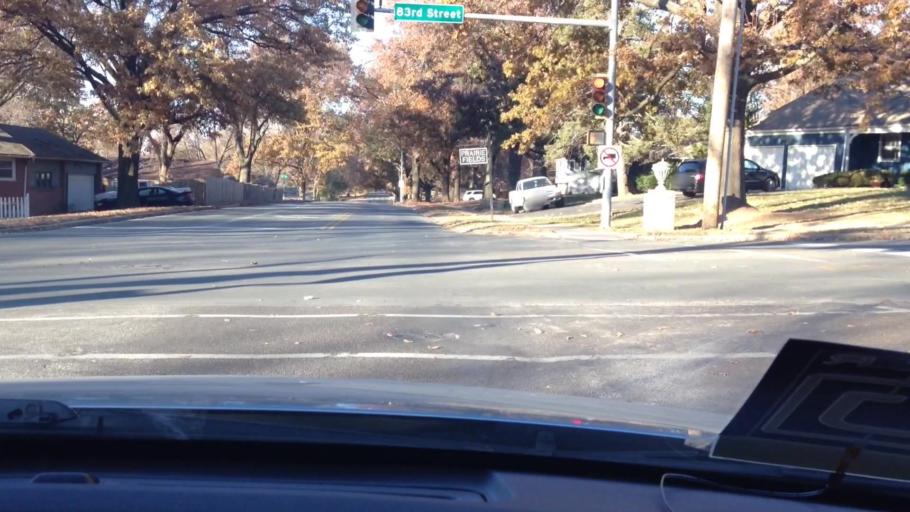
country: US
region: Kansas
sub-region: Johnson County
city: Overland Park
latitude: 38.9785
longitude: -94.6583
